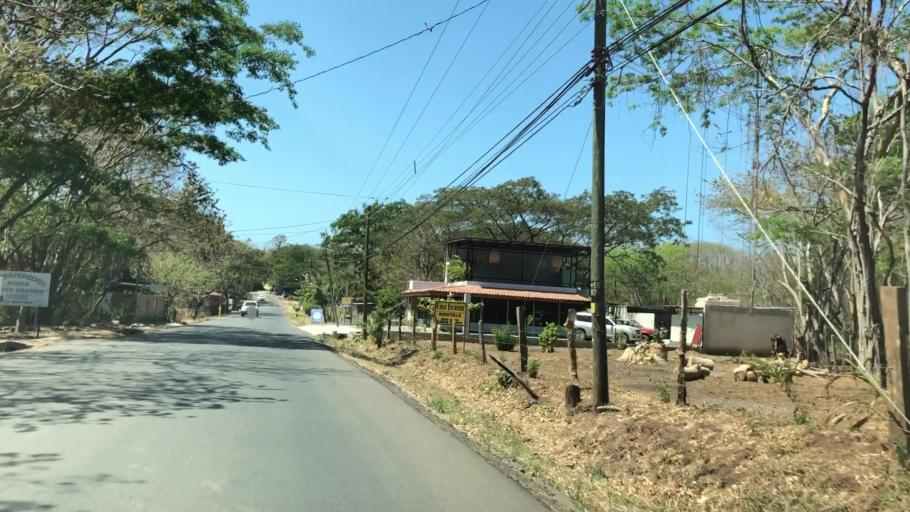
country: CR
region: Guanacaste
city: Sardinal
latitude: 10.3433
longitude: -85.8439
